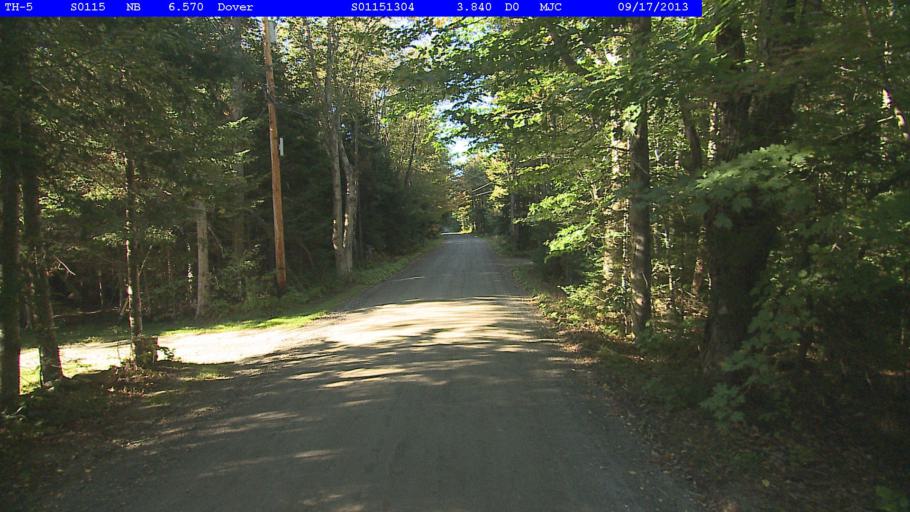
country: US
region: Vermont
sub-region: Windham County
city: Dover
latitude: 42.9786
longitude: -72.8932
